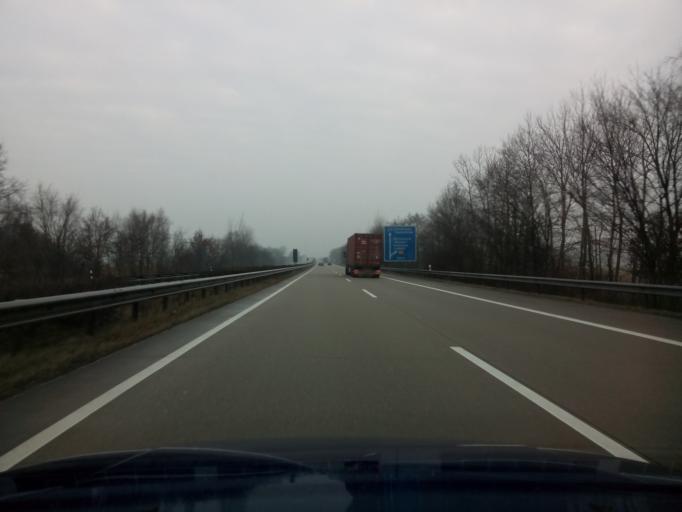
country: DE
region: Lower Saxony
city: Loxstedt
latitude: 53.4895
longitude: 8.6238
